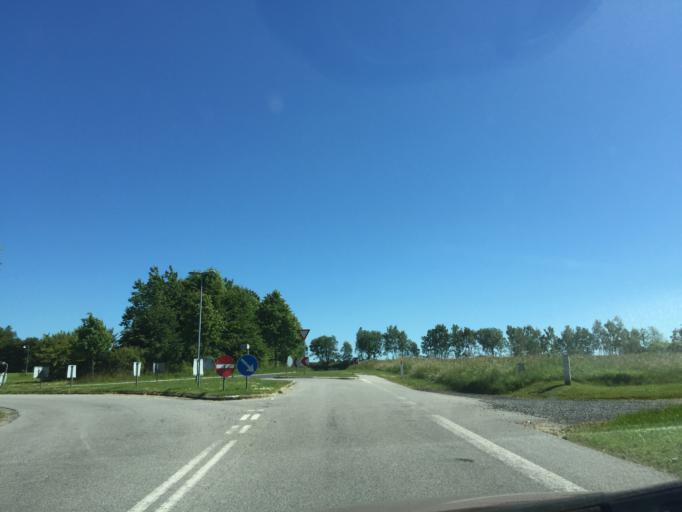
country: DK
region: Central Jutland
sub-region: Viborg Kommune
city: Bjerringbro
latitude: 56.3579
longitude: 9.6673
